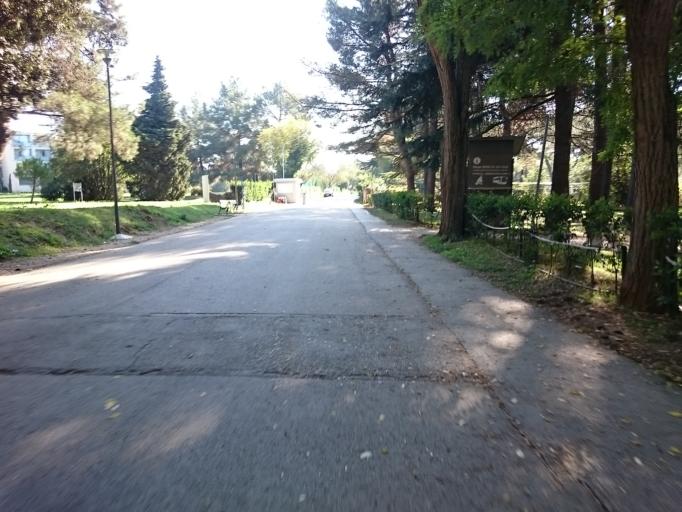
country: HR
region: Istarska
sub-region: Grad Porec
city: Porec
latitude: 45.2353
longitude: 13.5978
